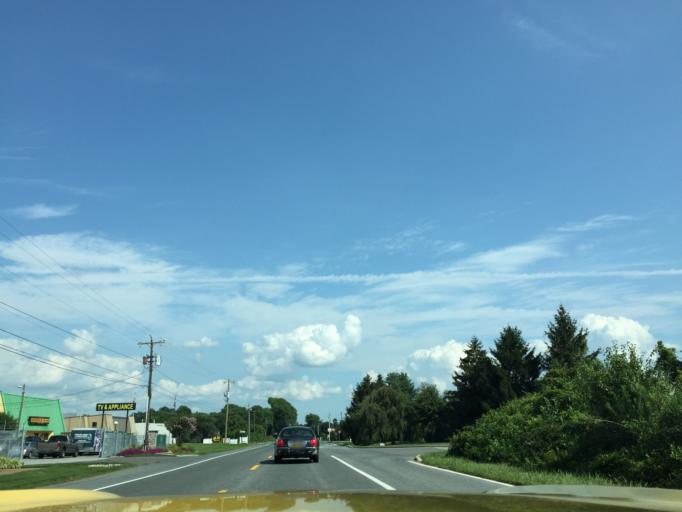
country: US
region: Delaware
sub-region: New Castle County
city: Wilmington Manor
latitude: 39.6721
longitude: -75.6182
